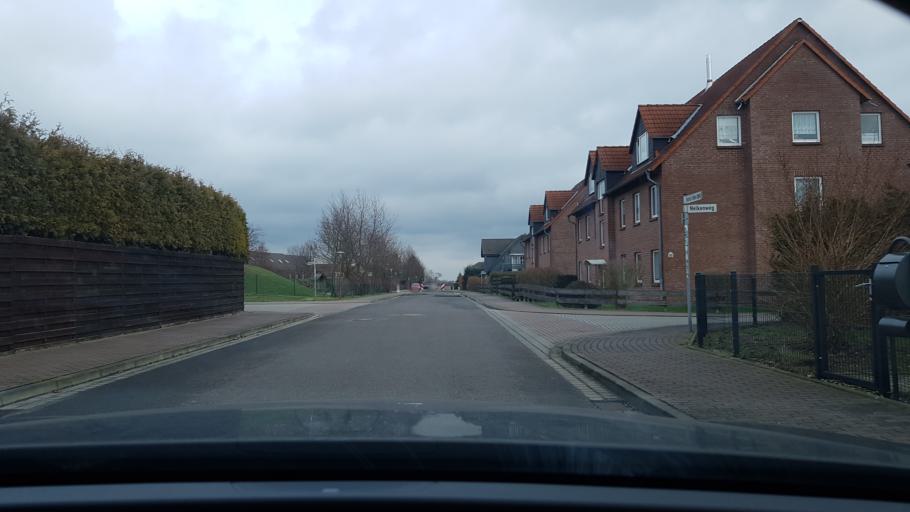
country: DE
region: Saxony-Anhalt
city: Oebisfelde
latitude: 52.4322
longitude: 10.9999
